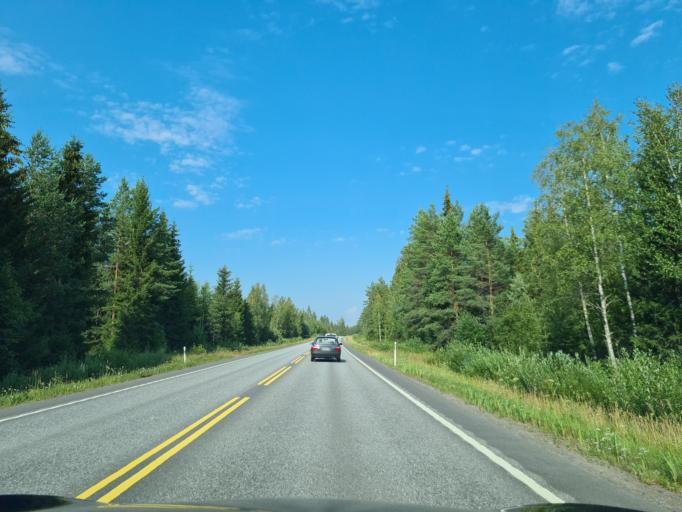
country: FI
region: Satakunta
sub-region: Pori
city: Laengelmaeki
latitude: 61.7622
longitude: 22.1436
